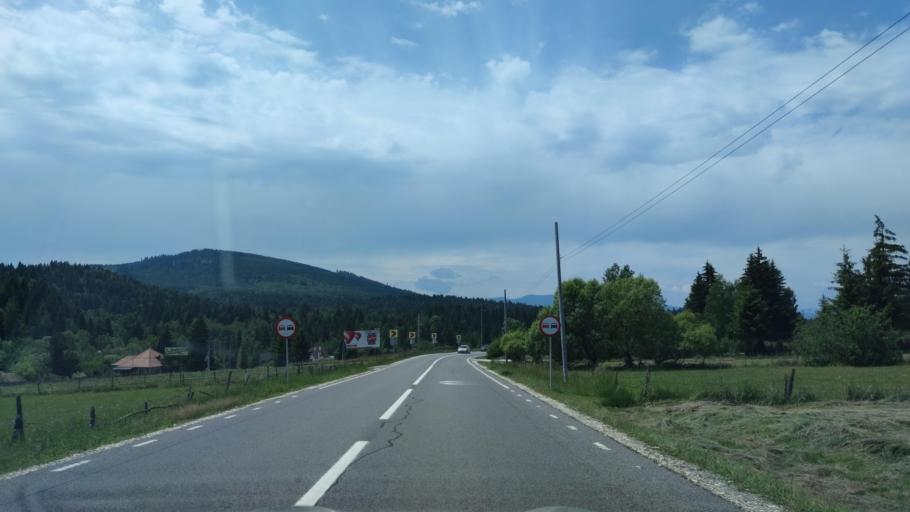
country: RO
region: Harghita
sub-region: Comuna Voslobeni
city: Voslobeni
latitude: 46.6196
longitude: 25.6999
